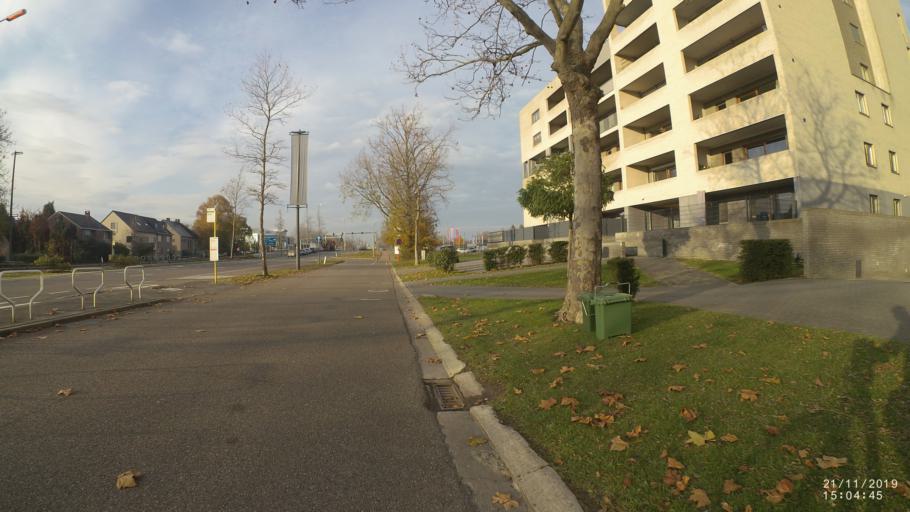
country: BE
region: Flanders
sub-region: Provincie Limburg
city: Hasselt
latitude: 50.9233
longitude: 5.3194
